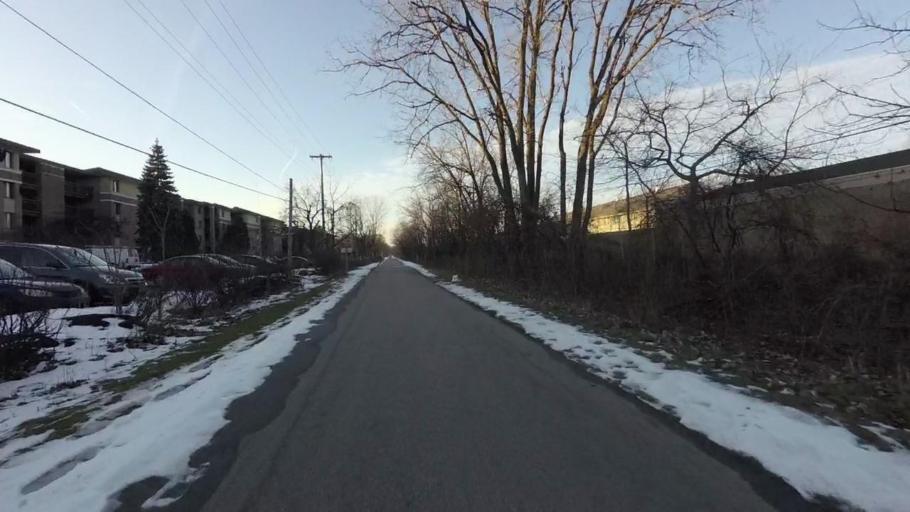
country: US
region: Wisconsin
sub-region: Milwaukee County
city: Whitefish Bay
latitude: 43.1043
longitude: -87.9095
